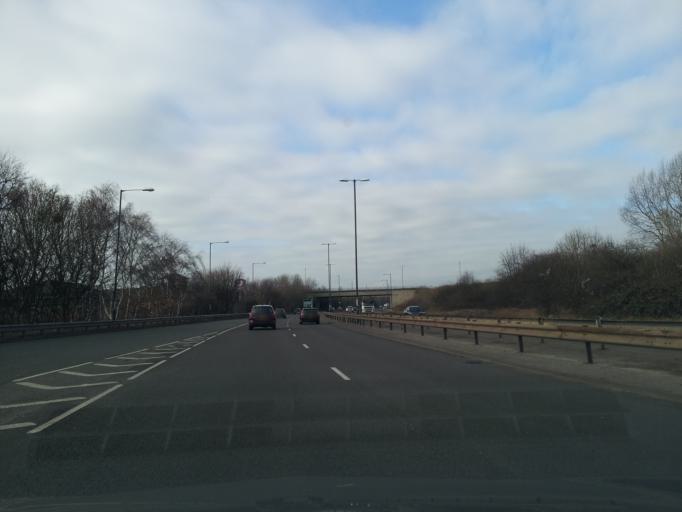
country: GB
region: England
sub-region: Derbyshire
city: Borrowash
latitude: 52.9156
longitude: -1.4285
